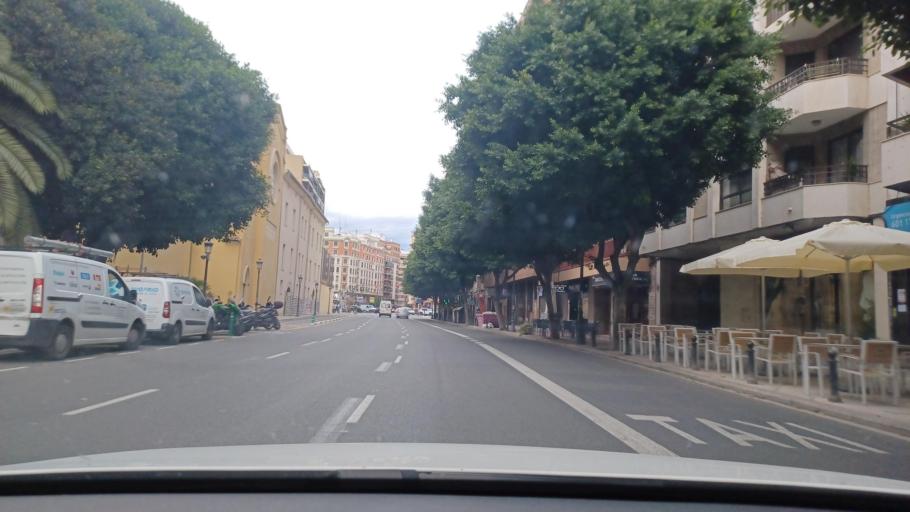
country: ES
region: Valencia
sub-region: Provincia de Valencia
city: Valencia
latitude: 39.4637
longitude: -0.3819
